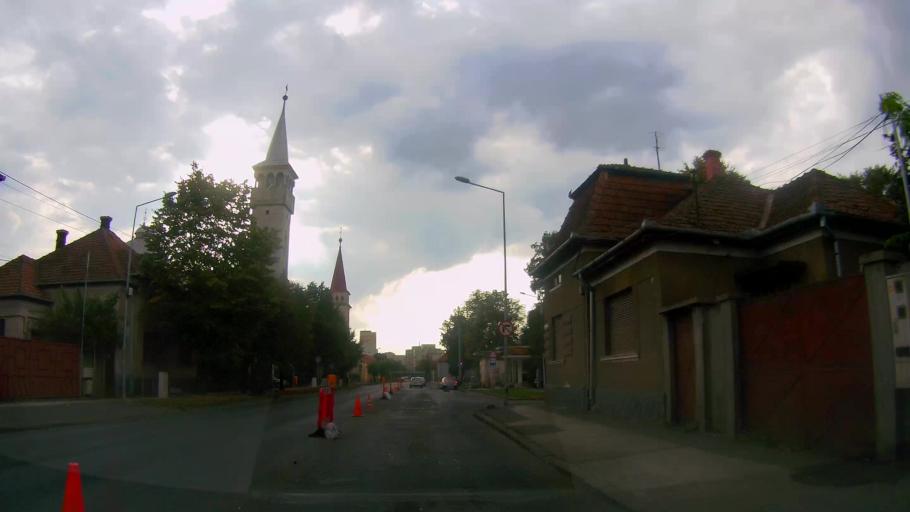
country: RO
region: Satu Mare
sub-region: Municipiul Satu Mare
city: Satu Mare
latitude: 47.7828
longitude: 22.8762
